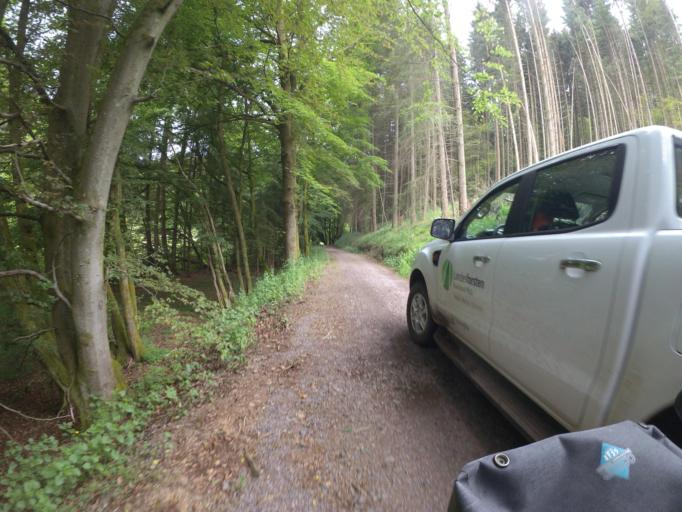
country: DE
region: Rheinland-Pfalz
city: Trulben
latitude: 49.1237
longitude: 7.5418
